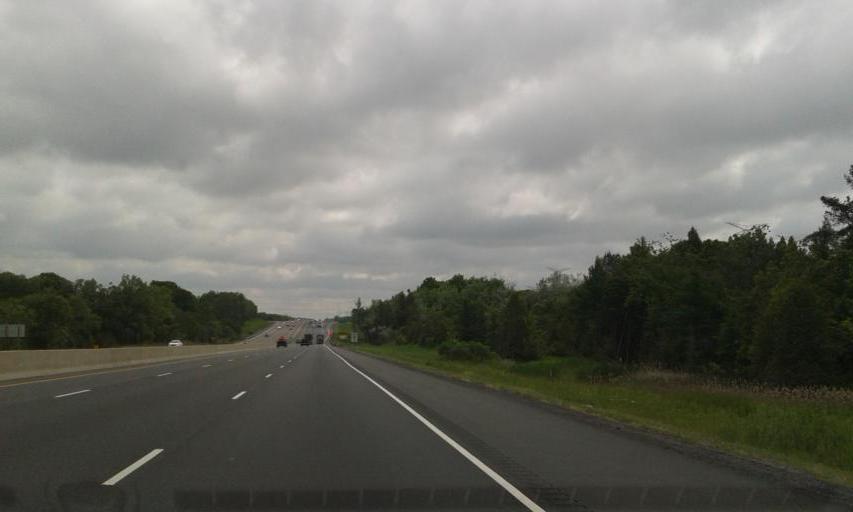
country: CA
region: Ontario
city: Cobourg
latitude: 43.9272
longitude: -78.5060
